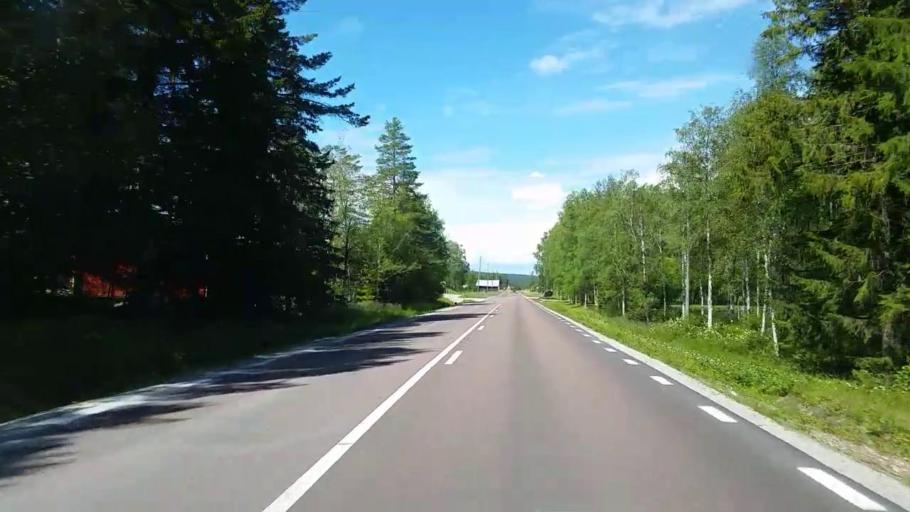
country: SE
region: Dalarna
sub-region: Rattviks Kommun
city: Raettvik
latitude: 61.0361
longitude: 15.2017
